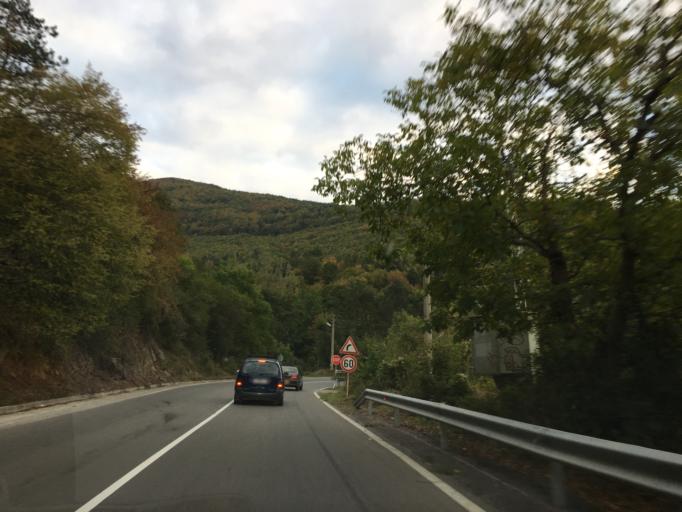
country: BG
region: Sofiya
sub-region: Obshtina Svoge
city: Svoge
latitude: 42.9334
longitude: 23.3880
